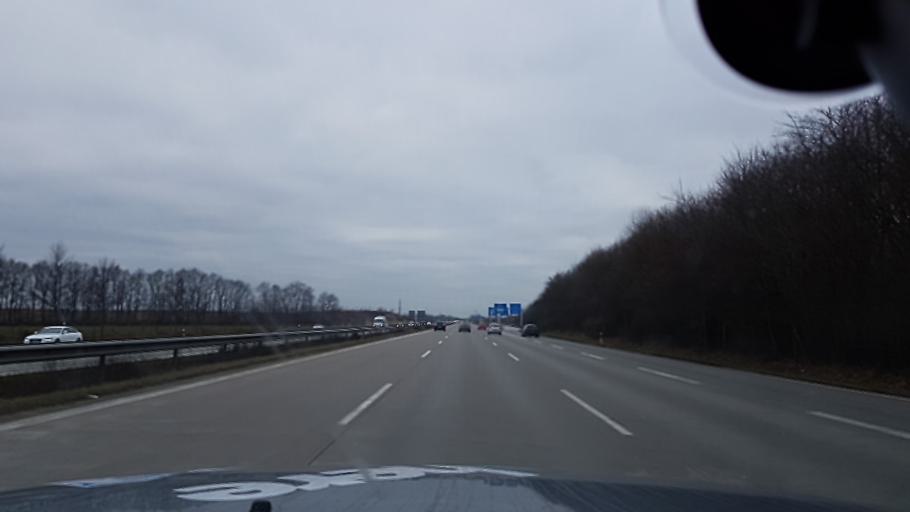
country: DE
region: Schleswig-Holstein
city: Hamberge
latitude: 53.8542
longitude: 10.6020
